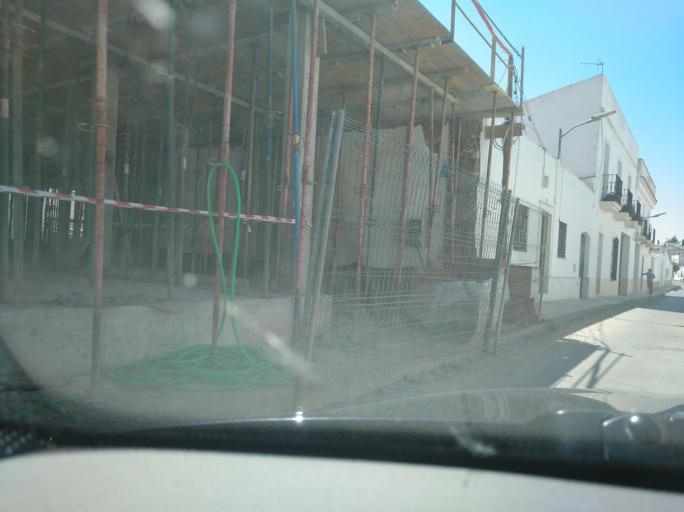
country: ES
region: Extremadura
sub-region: Provincia de Badajoz
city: Olivenza
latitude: 38.6812
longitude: -7.1016
